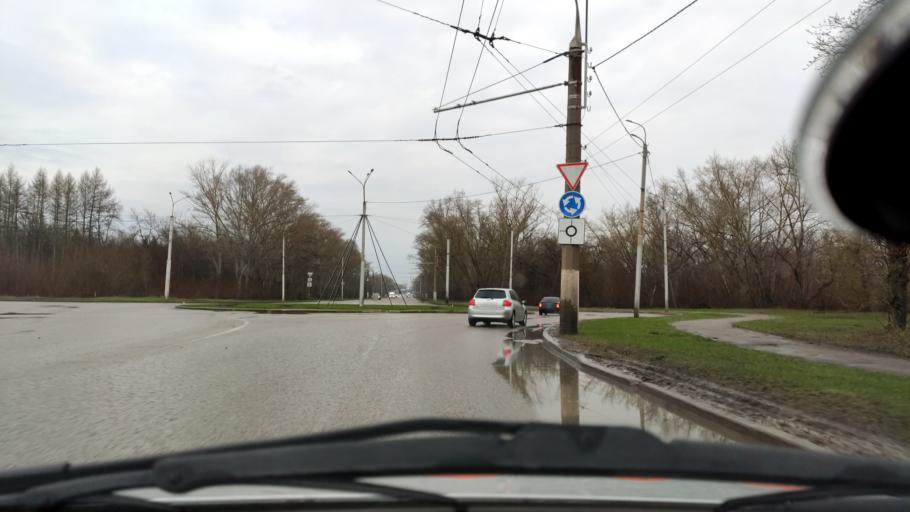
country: RU
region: Bashkortostan
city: Sterlitamak
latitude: 53.6561
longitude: 55.9486
